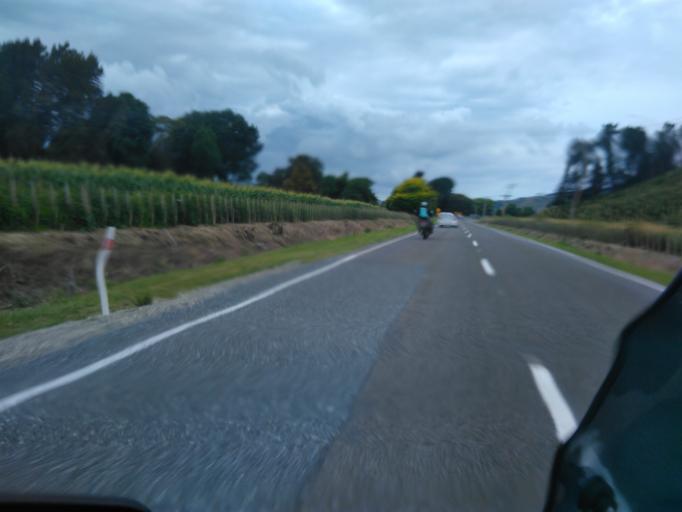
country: NZ
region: Gisborne
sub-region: Gisborne District
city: Gisborne
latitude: -38.4676
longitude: 177.8205
